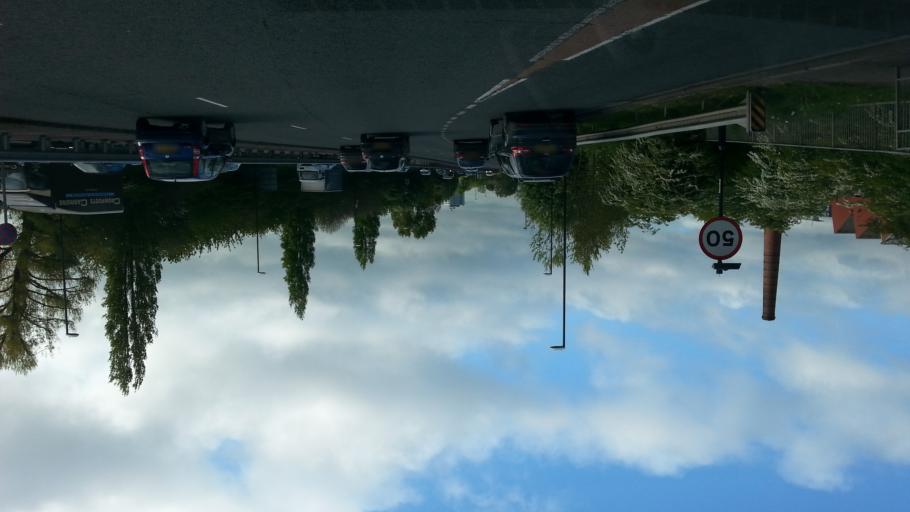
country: GB
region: England
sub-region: Coventry
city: Coventry
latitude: 52.4227
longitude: -1.4871
